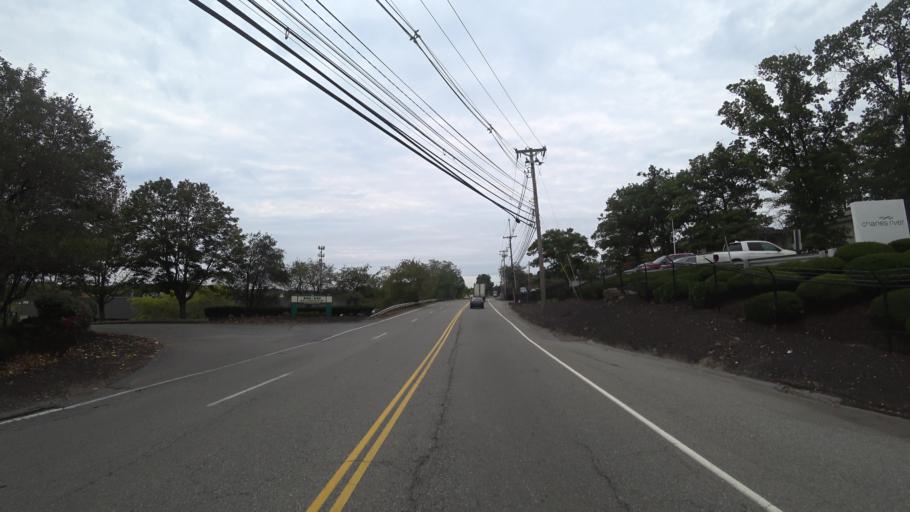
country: US
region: Massachusetts
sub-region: Middlesex County
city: Wilmington
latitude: 42.5930
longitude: -71.1611
